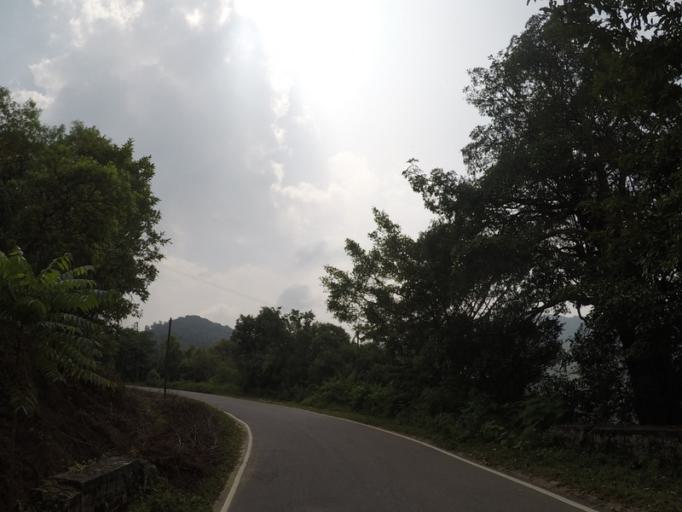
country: IN
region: Karnataka
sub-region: Chikmagalur
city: Mudigere
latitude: 13.1969
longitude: 75.4091
